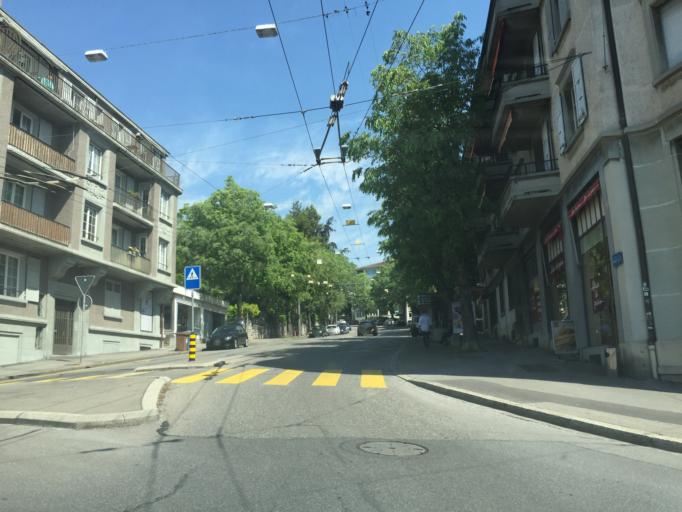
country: CH
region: Vaud
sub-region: Lausanne District
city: Lausanne
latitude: 46.5111
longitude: 6.6373
